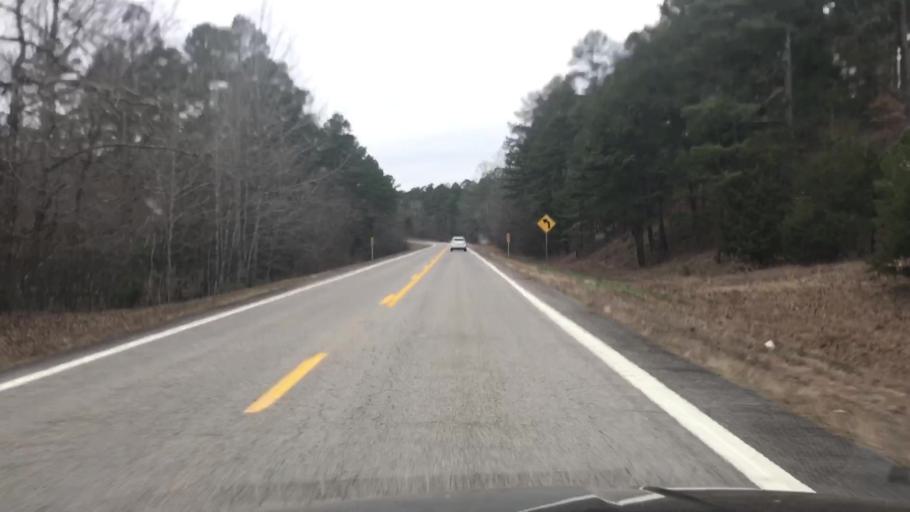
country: US
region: Arkansas
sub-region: Montgomery County
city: Mount Ida
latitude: 34.6862
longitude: -93.8588
